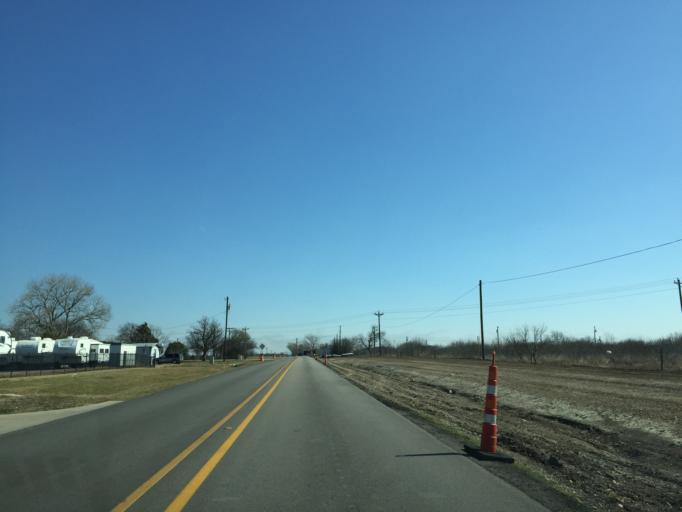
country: US
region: Texas
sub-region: Williamson County
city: Serenada
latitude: 30.7236
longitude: -97.6419
